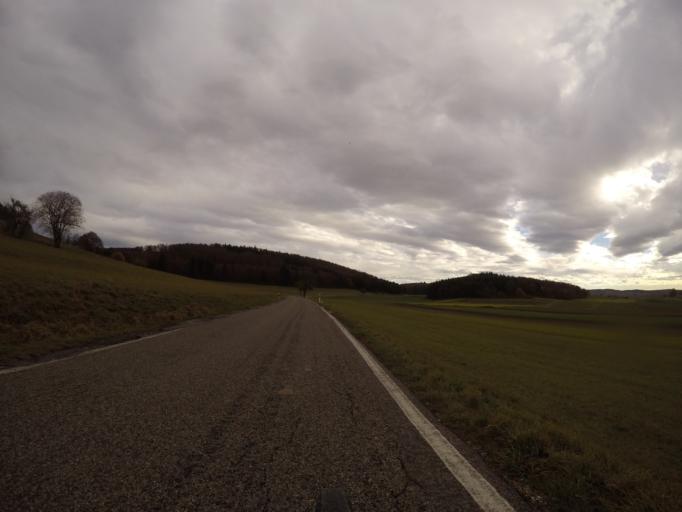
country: DE
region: Baden-Wuerttemberg
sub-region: Tuebingen Region
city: Sankt Johann
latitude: 48.4168
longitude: 9.2881
